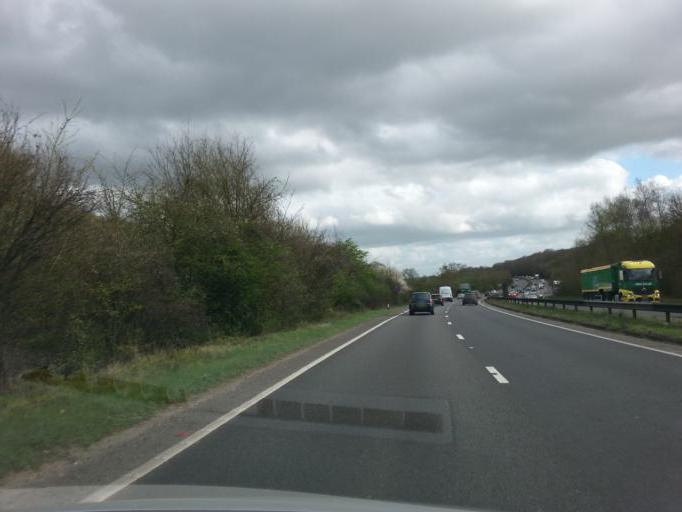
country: GB
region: England
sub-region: Hampshire
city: Andover
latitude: 51.1959
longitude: -1.4245
